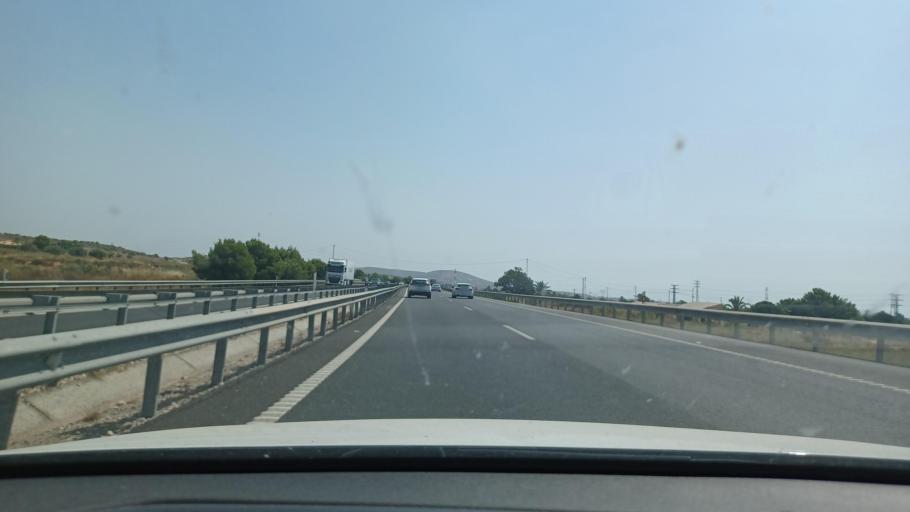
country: ES
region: Valencia
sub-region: Provincia de Alicante
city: Elche
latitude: 38.3018
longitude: -0.6320
